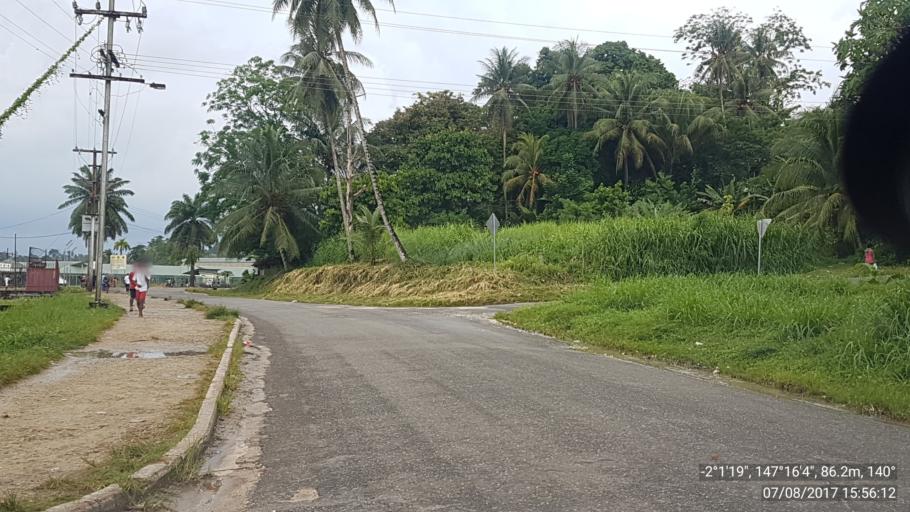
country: PG
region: Manus
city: Lorengau
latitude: -2.0222
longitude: 147.2678
